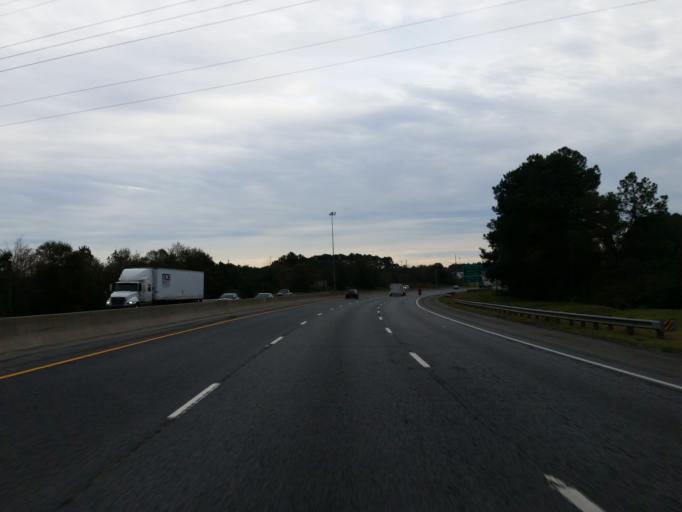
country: US
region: Georgia
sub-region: Tift County
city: Unionville
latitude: 31.4225
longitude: -83.5082
